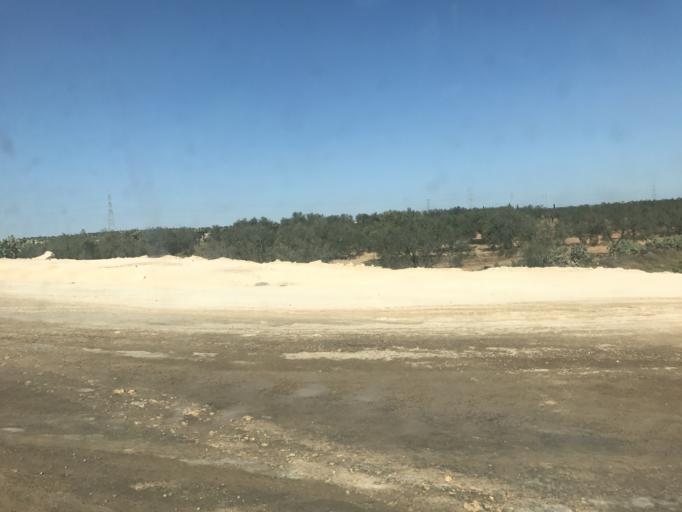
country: TN
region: Susah
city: Masakin
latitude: 35.7771
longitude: 10.5589
